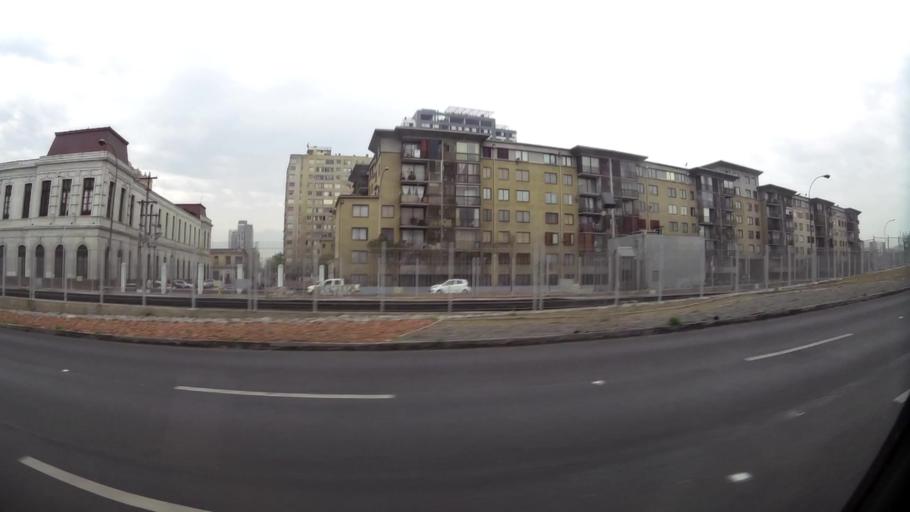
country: CL
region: Santiago Metropolitan
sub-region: Provincia de Santiago
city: Santiago
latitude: -33.4582
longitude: -70.6570
